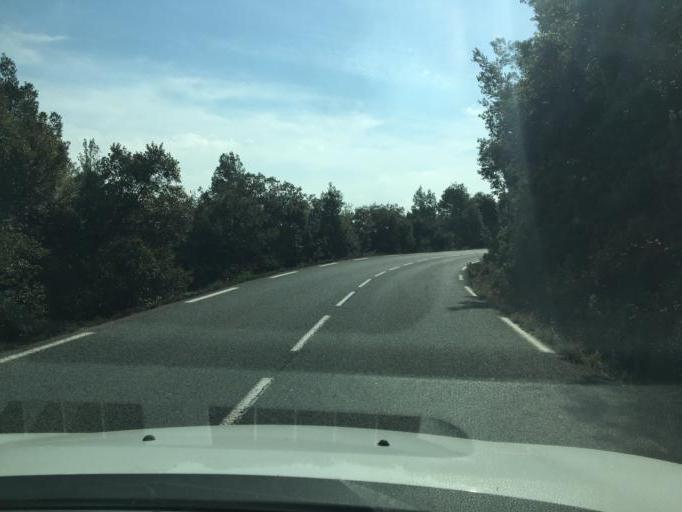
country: FR
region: Provence-Alpes-Cote d'Azur
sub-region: Departement du Var
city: Bargemon
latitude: 43.6095
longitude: 6.5519
